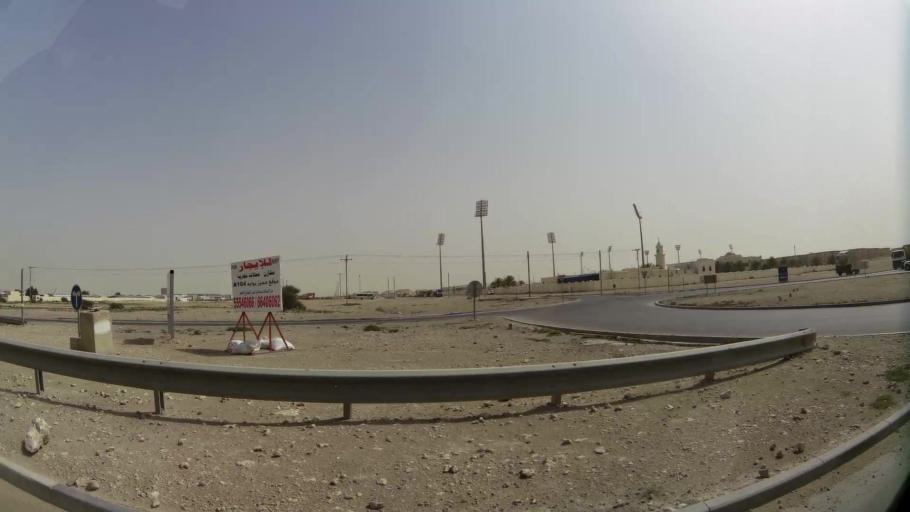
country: QA
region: Baladiyat ar Rayyan
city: Ar Rayyan
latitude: 25.2181
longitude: 51.3553
